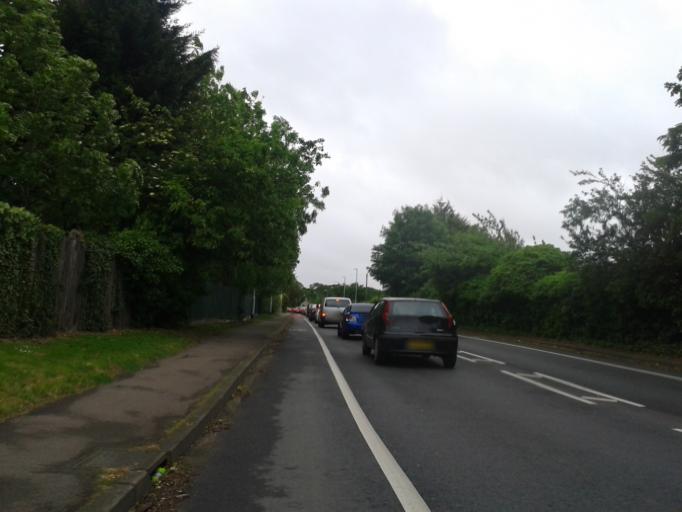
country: GB
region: England
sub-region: Cambridgeshire
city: Histon
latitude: 52.2474
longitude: 0.1096
